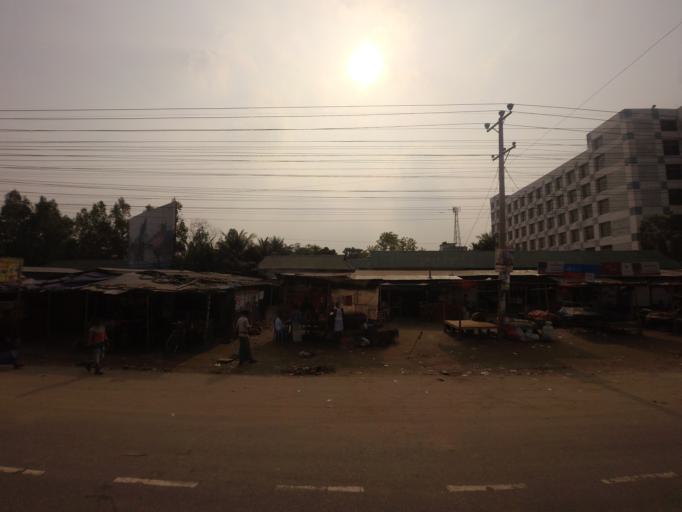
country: BD
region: Dhaka
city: Tungi
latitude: 23.9859
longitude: 90.2594
